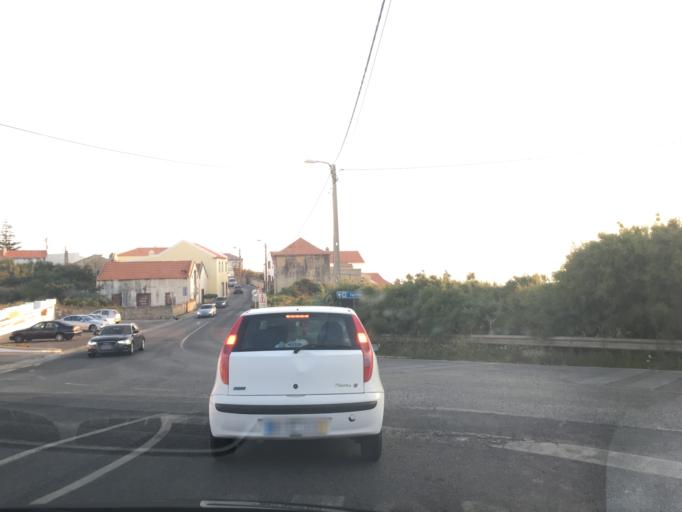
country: PT
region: Lisbon
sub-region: Sintra
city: Colares
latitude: 38.8378
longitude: -9.4635
